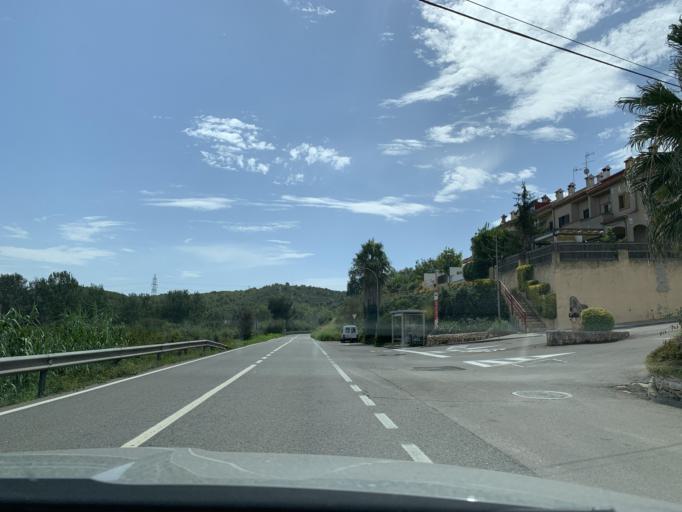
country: ES
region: Catalonia
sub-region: Provincia de Tarragona
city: Altafulla
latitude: 41.1575
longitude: 1.3636
